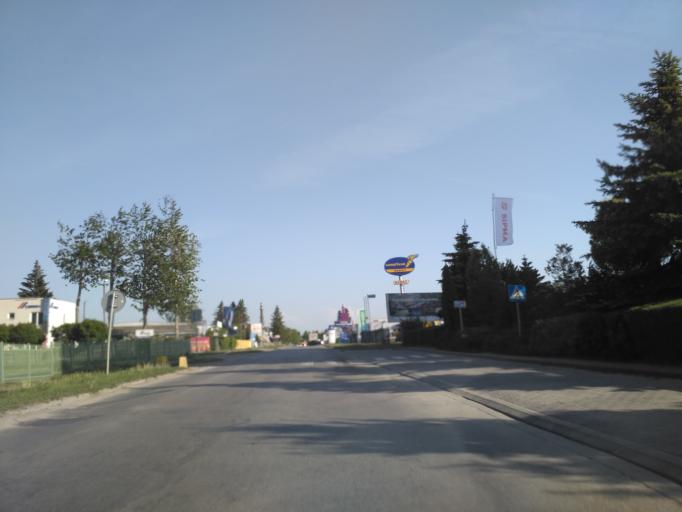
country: PL
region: Lublin Voivodeship
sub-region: Powiat lubelski
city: Lublin
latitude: 51.2096
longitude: 22.5610
